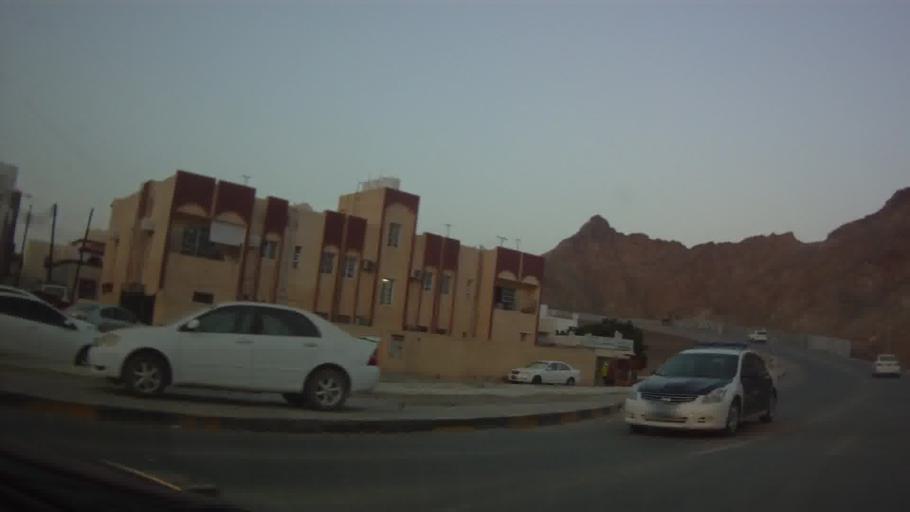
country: OM
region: Muhafazat Masqat
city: Muscat
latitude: 23.6303
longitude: 58.5426
